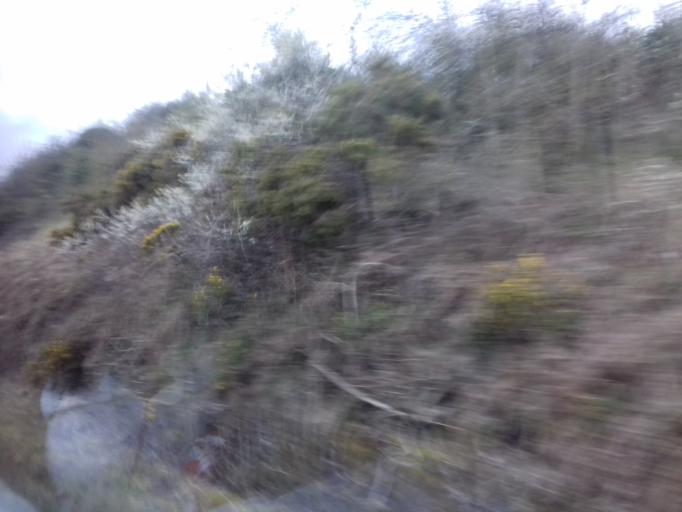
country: IE
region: Leinster
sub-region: An Iarmhi
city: Kinnegad
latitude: 53.4853
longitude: -7.1044
